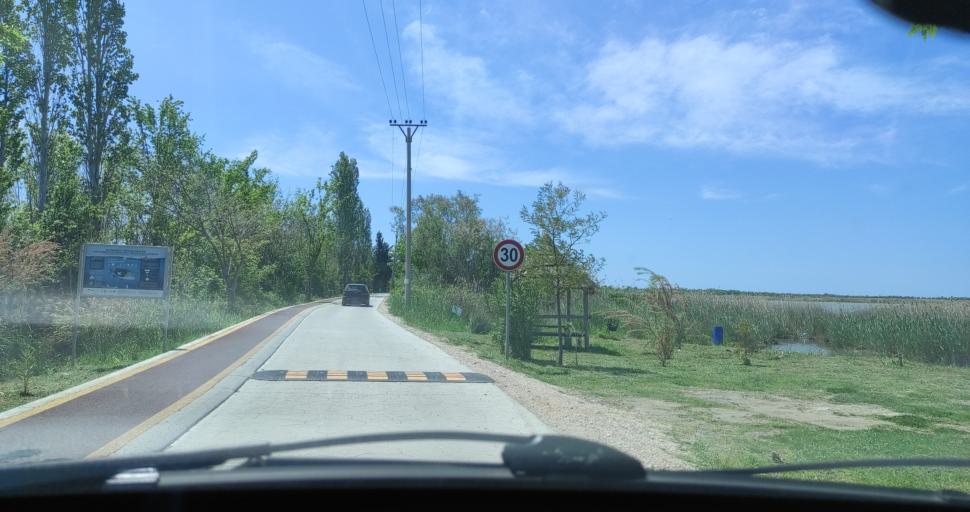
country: AL
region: Lezhe
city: Lezhe
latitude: 41.7520
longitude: 19.6070
